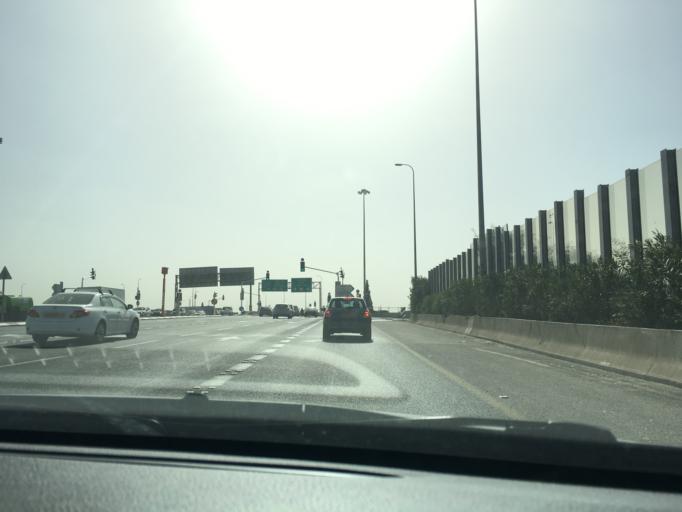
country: IL
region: Central District
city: Kfar Saba
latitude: 32.1655
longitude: 34.9267
